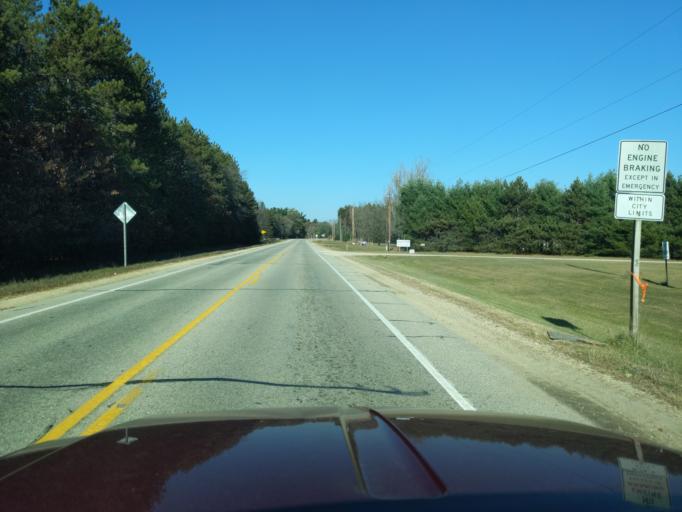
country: US
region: Wisconsin
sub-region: Waushara County
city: Wautoma
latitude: 44.0589
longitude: -89.2946
